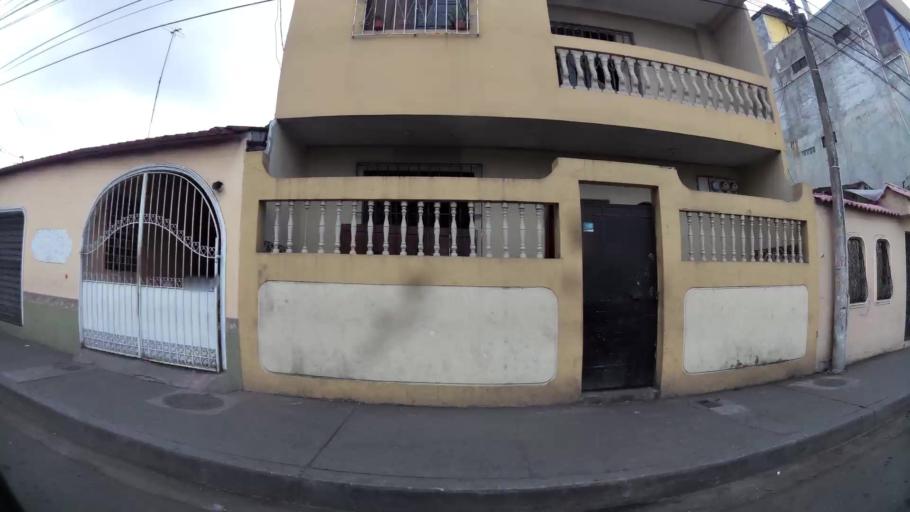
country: EC
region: Guayas
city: Guayaquil
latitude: -2.2300
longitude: -79.9011
